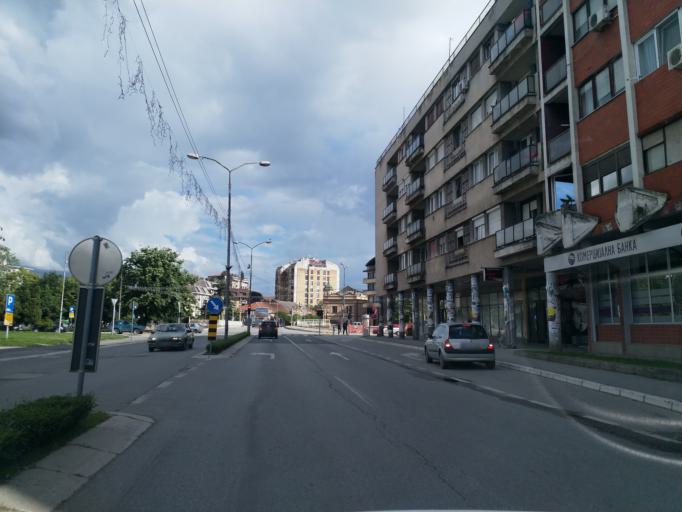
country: RS
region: Central Serbia
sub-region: Pomoravski Okrug
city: Paracin
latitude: 43.8638
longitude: 21.4093
